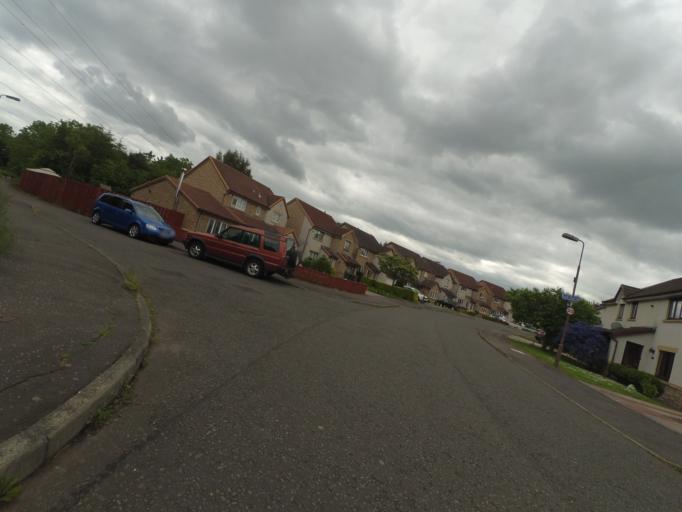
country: GB
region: Scotland
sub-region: East Lothian
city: Musselburgh
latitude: 55.9377
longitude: -3.0950
